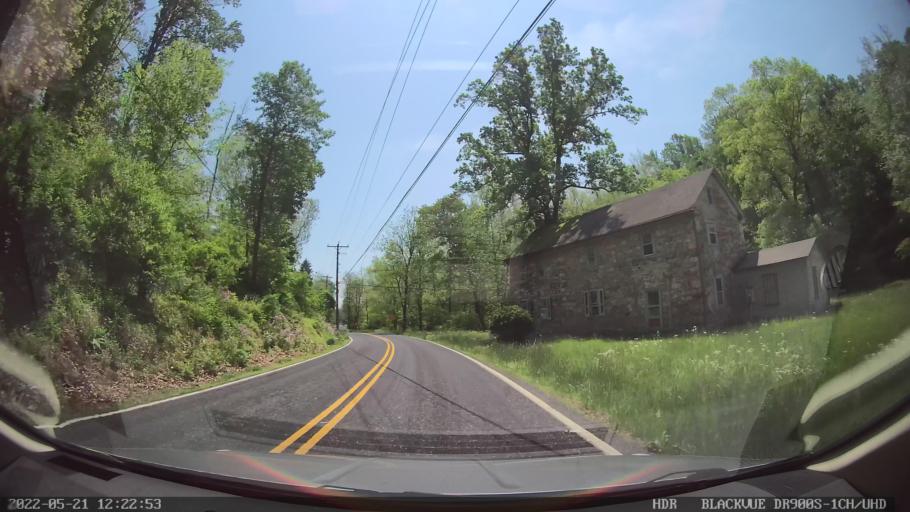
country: US
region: Pennsylvania
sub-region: Berks County
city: Bally
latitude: 40.3973
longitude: -75.6119
